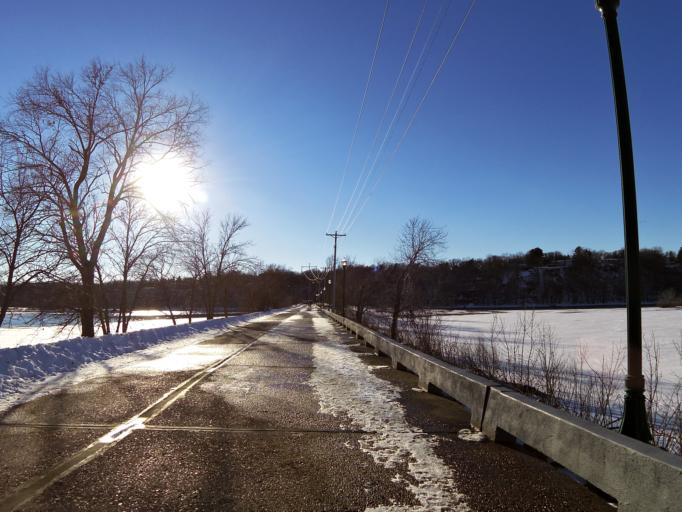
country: US
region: Wisconsin
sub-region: Saint Croix County
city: Hudson
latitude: 44.9726
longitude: -92.7644
